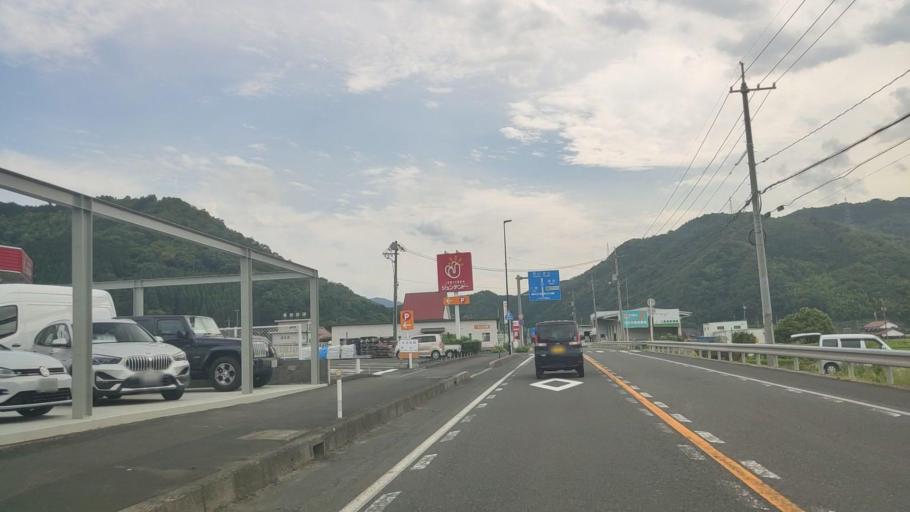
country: JP
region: Tottori
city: Tottori
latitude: 35.3565
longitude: 134.2077
